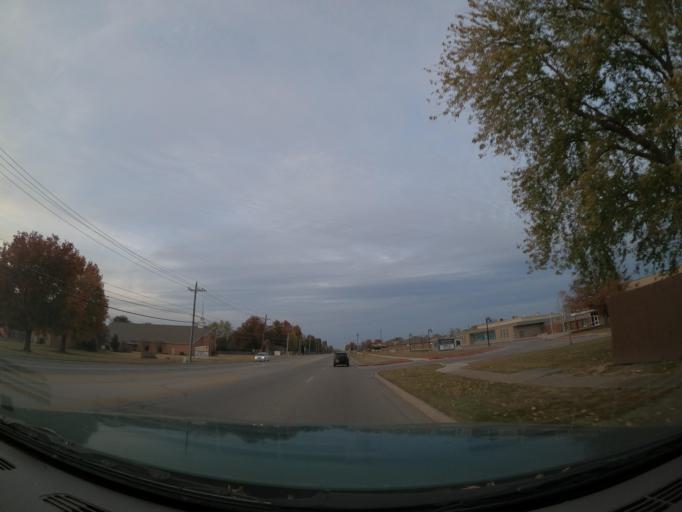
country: US
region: Oklahoma
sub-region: Tulsa County
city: Broken Arrow
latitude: 36.0233
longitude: -95.7974
